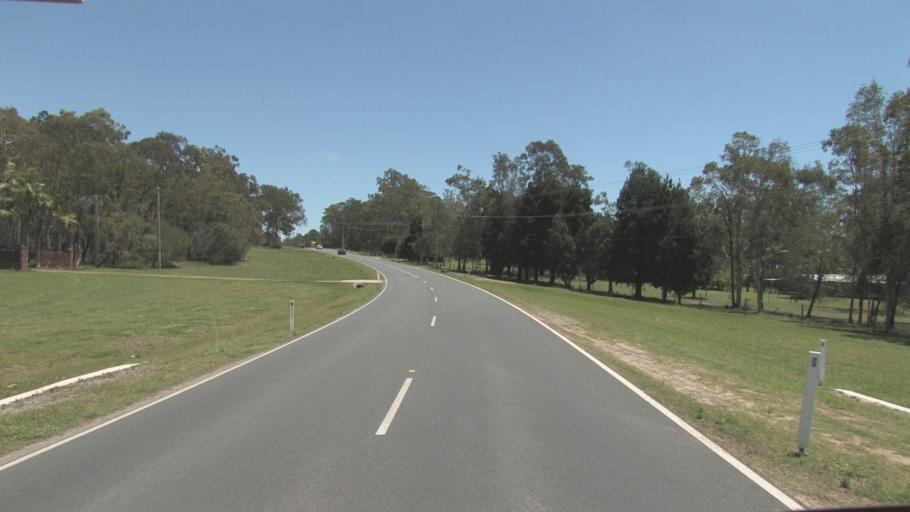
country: AU
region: Queensland
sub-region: Logan
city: Park Ridge South
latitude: -27.7014
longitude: 153.0589
